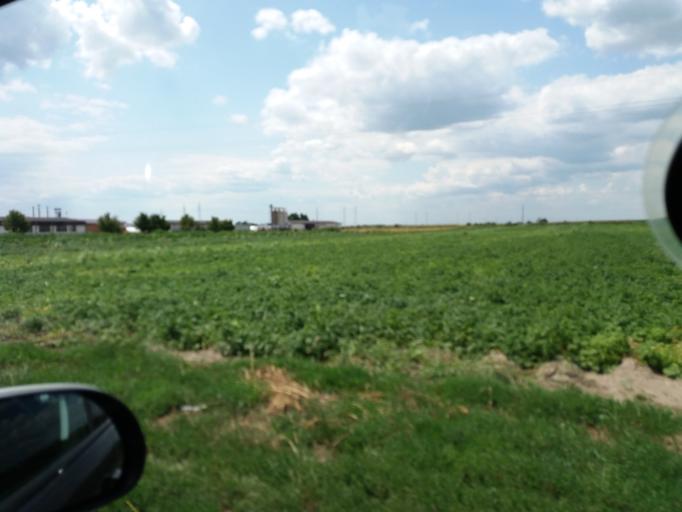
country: RS
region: Autonomna Pokrajina Vojvodina
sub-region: Sremski Okrug
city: Pecinci
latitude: 44.8946
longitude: 19.9656
